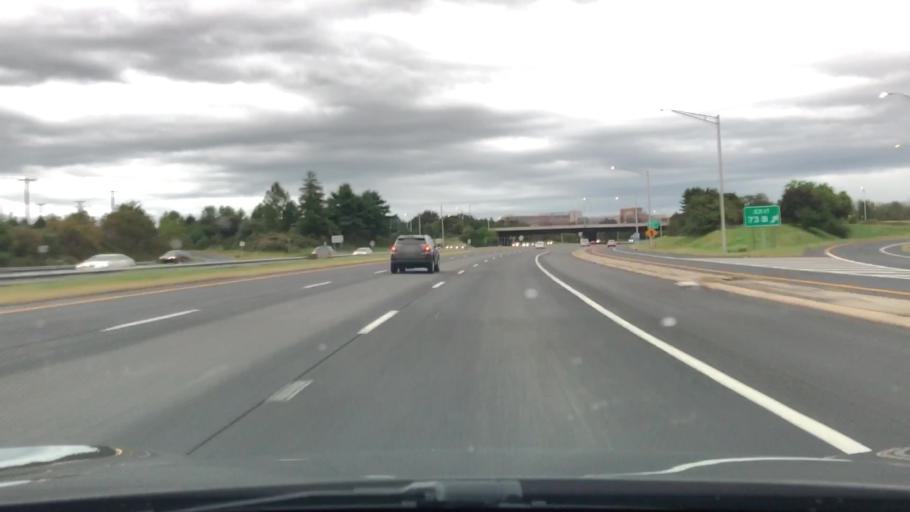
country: US
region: New Jersey
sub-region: Mercer County
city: Ewing
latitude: 40.2881
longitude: -74.8151
